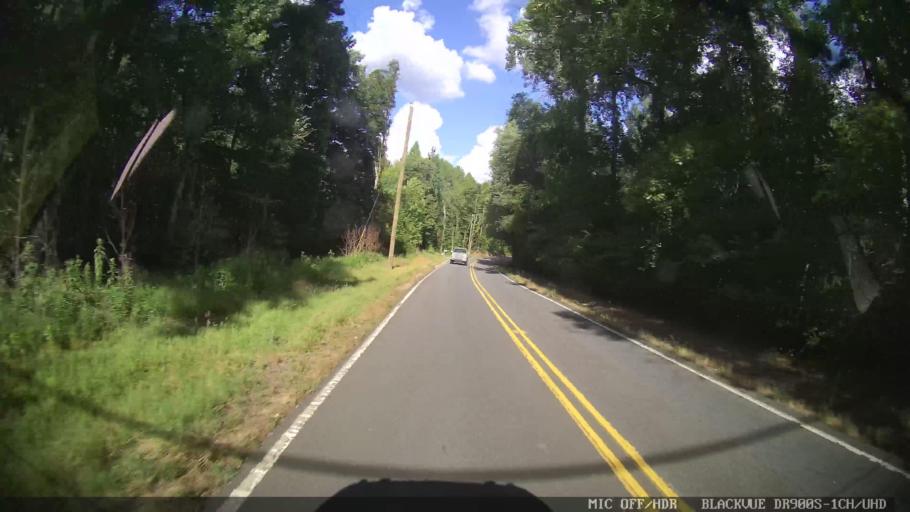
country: US
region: Georgia
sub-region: Floyd County
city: Lindale
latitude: 34.1910
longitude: -85.0597
